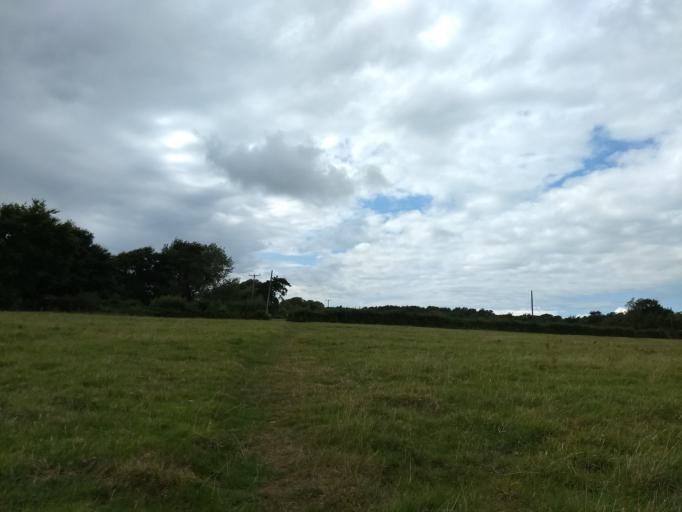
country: GB
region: England
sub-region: Isle of Wight
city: Newport
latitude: 50.7048
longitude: -1.3061
